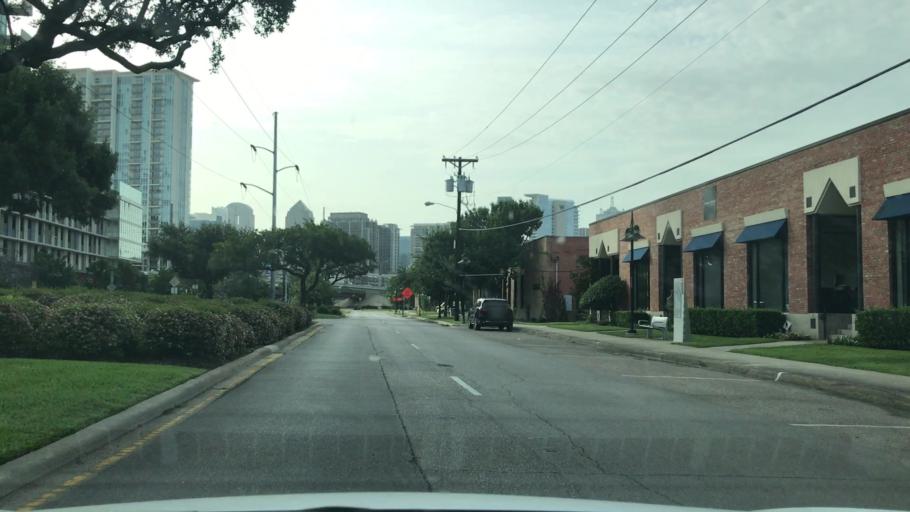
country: US
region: Texas
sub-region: Dallas County
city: Dallas
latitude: 32.7952
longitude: -96.8176
